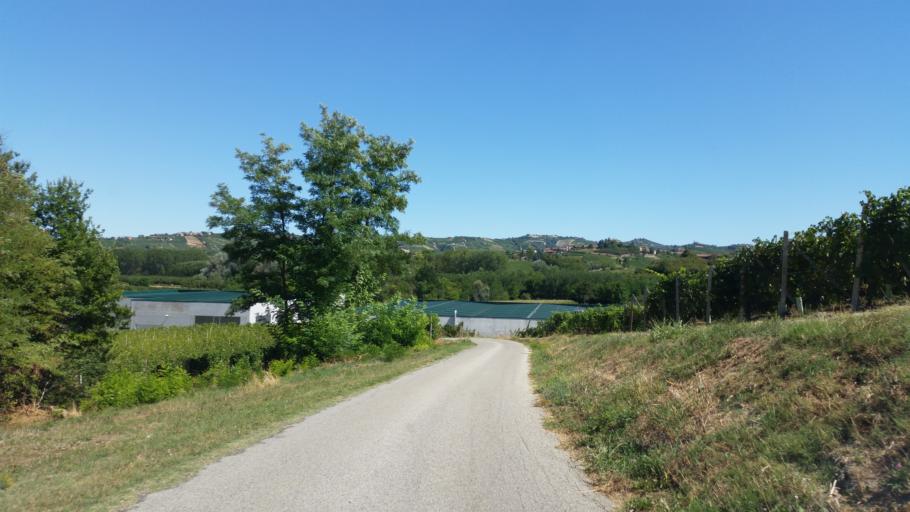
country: IT
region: Piedmont
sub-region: Provincia di Cuneo
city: Neive-Borgonovo
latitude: 44.7371
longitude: 8.1251
